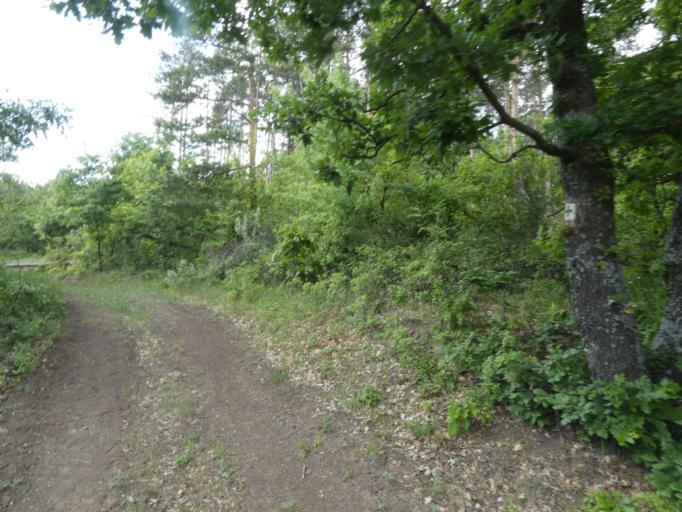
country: HU
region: Nograd
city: Szurdokpuspoki
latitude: 47.8558
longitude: 19.7242
